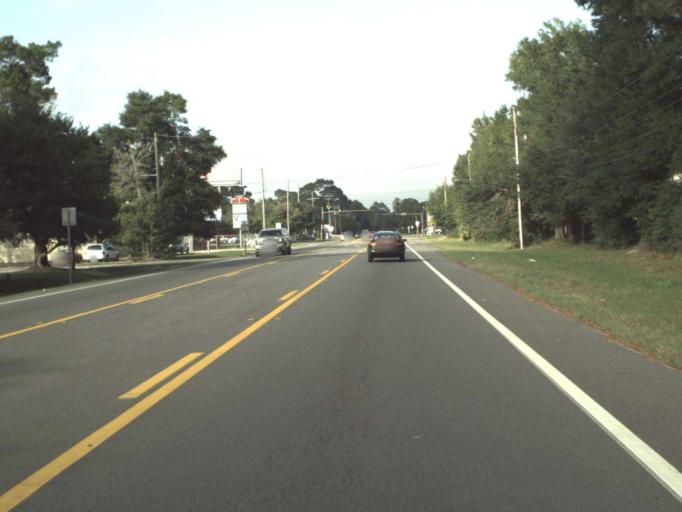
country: US
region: Florida
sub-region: Escambia County
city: Myrtle Grove
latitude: 30.4191
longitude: -87.3173
